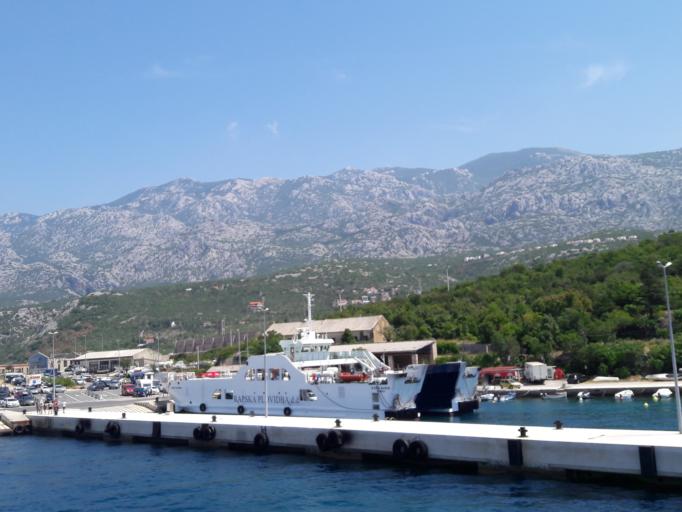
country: HR
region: Primorsko-Goranska
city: Banjol
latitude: 44.7194
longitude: 14.8903
